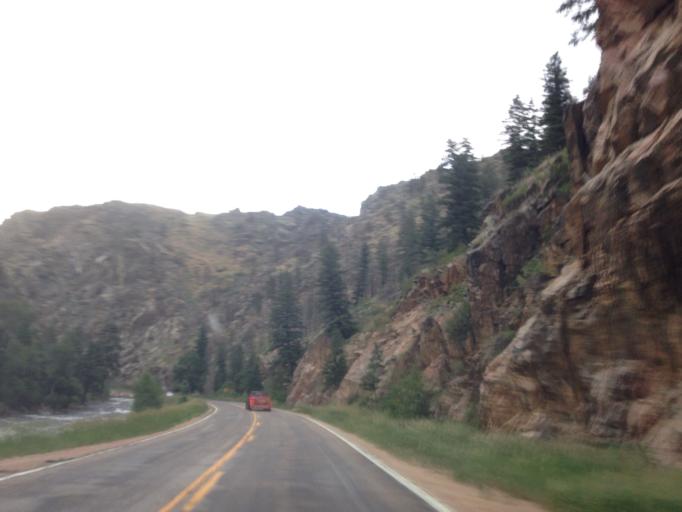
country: US
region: Colorado
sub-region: Larimer County
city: Laporte
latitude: 40.6854
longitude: -105.3782
